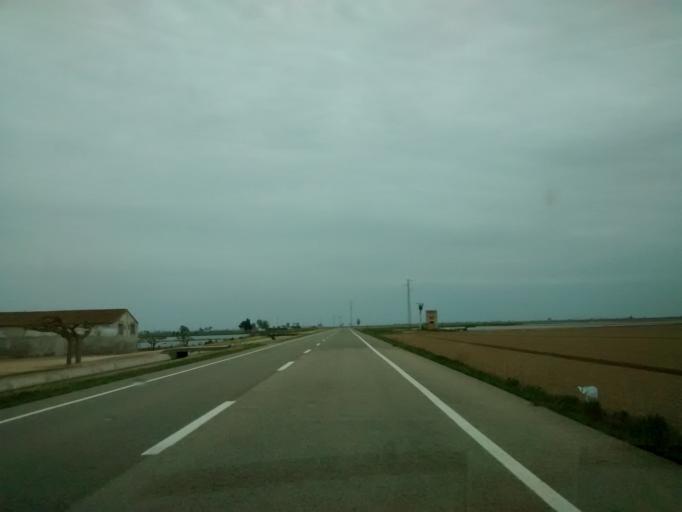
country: ES
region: Catalonia
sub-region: Provincia de Tarragona
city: Deltebre
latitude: 40.6962
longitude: 0.6801
